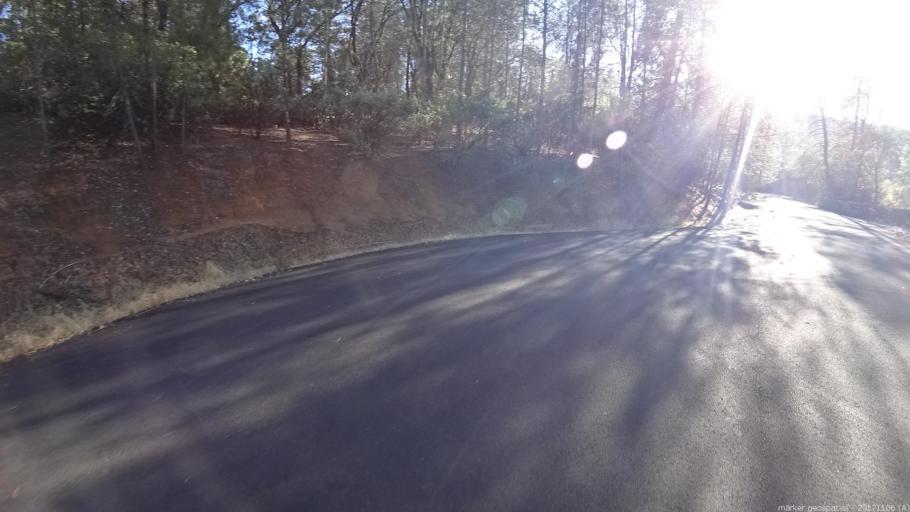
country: US
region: California
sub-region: Shasta County
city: Shasta
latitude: 40.5842
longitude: -122.4780
